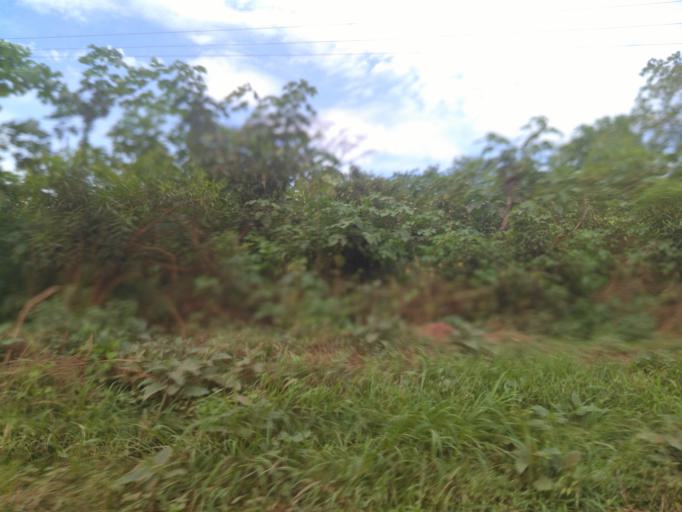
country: UG
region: Eastern Region
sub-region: Jinja District
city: Jinja
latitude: 0.4358
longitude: 33.1849
